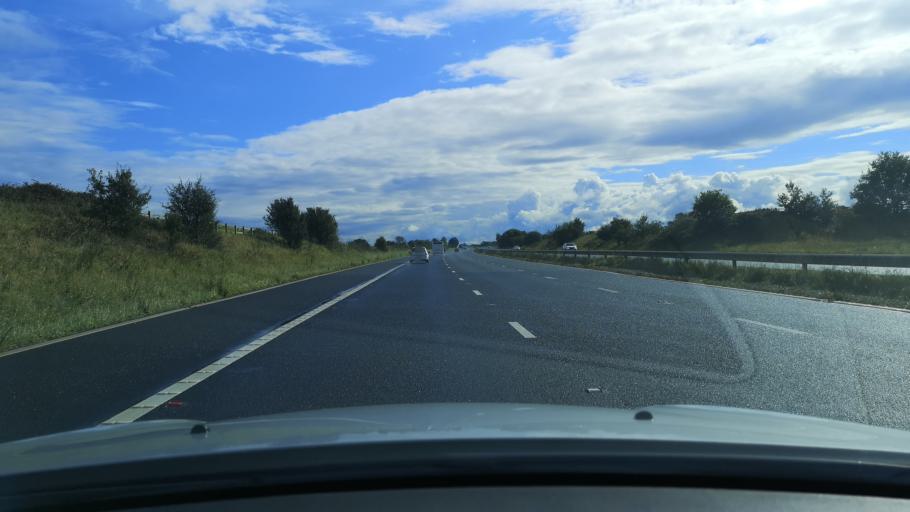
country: GB
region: England
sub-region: East Riding of Yorkshire
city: Pollington
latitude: 53.6923
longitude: -1.1135
